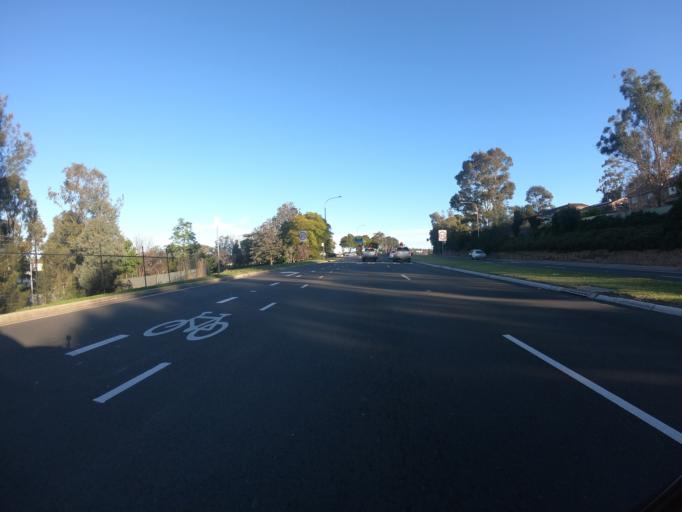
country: AU
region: New South Wales
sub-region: Campbelltown Municipality
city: Leumeah
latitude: -34.0442
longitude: 150.8297
